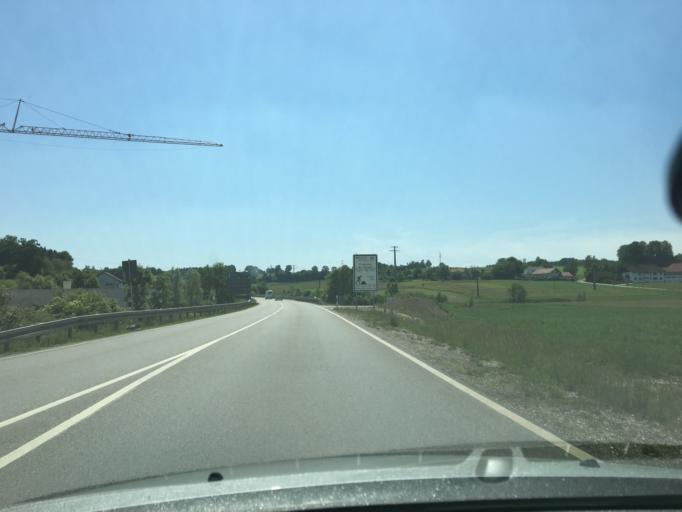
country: DE
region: Bavaria
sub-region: Upper Bavaria
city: Neumarkt-Sankt Veit
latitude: 48.3516
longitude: 12.4901
